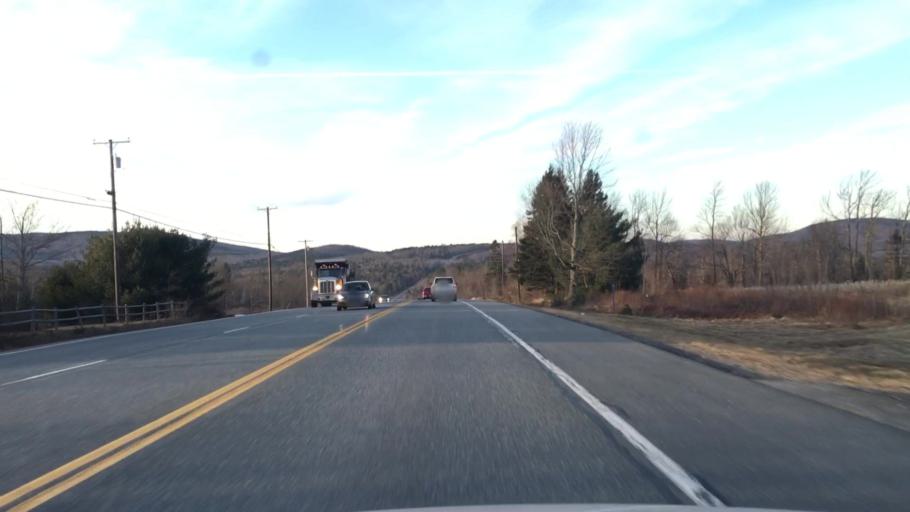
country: US
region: Maine
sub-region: Hancock County
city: Surry
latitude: 44.6261
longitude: -68.5351
